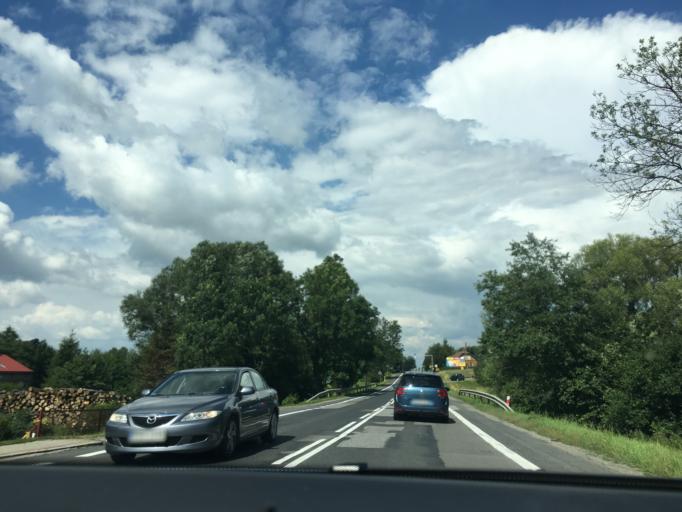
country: PL
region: Subcarpathian Voivodeship
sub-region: Powiat krosnienski
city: Dukla
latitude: 49.5934
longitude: 21.7144
